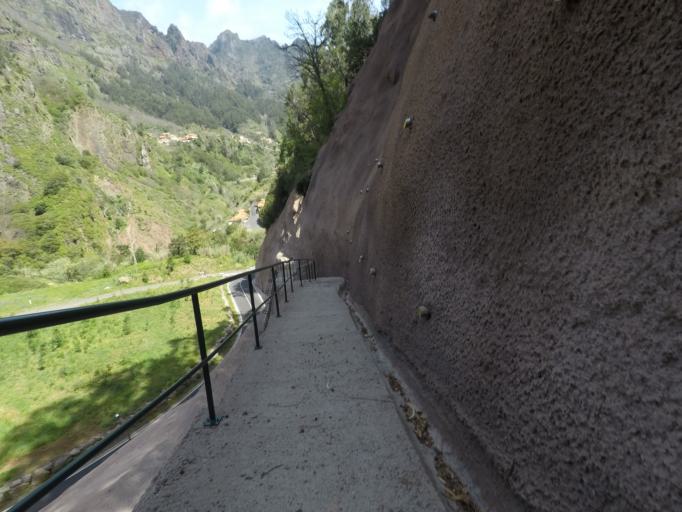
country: PT
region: Madeira
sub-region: Camara de Lobos
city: Curral das Freiras
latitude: 32.7260
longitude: -16.9652
